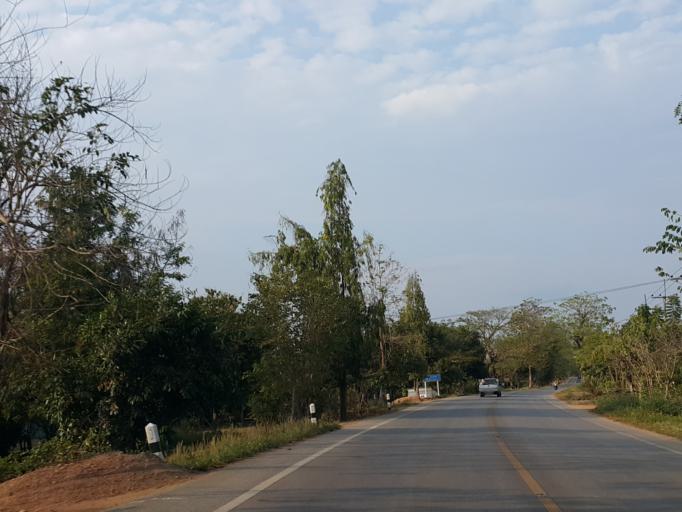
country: TH
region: Lampang
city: Lampang
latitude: 18.5008
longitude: 99.4718
